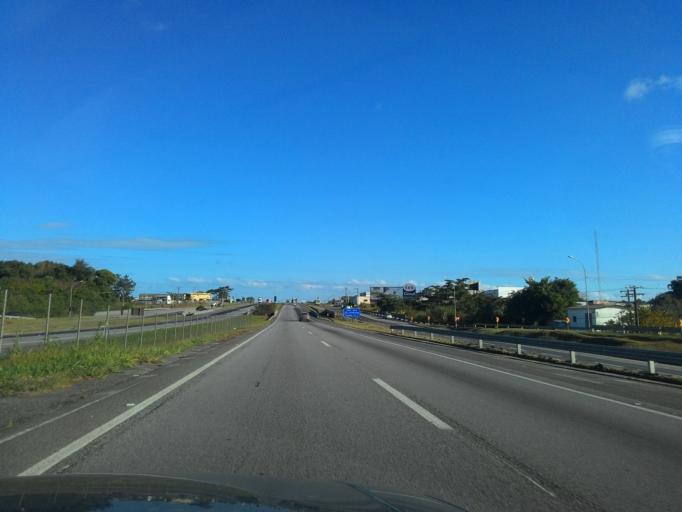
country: BR
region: Sao Paulo
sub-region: Registro
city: Registro
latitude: -24.5092
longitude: -47.8496
